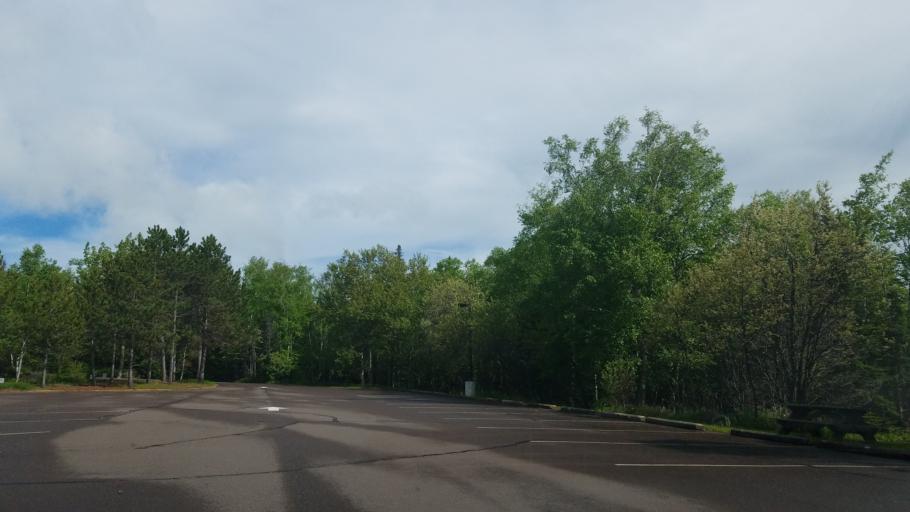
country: US
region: Minnesota
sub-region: Lake County
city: Silver Bay
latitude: 47.2015
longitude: -91.3668
